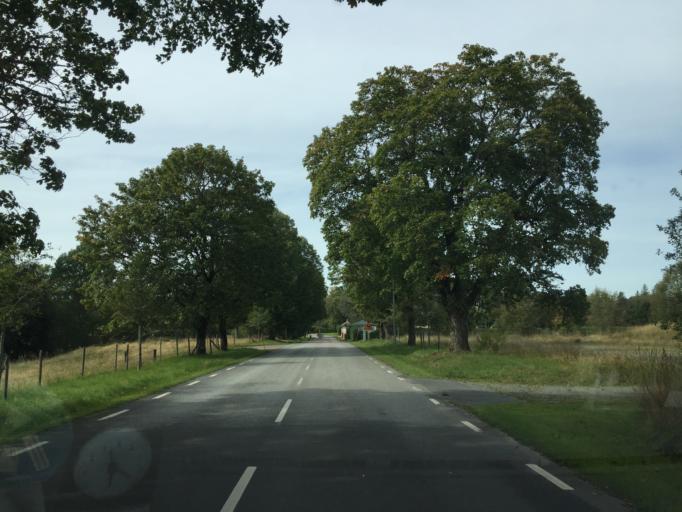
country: SE
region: Joenkoeping
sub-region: Varnamo Kommun
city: Varnamo
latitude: 57.2635
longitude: 14.0604
